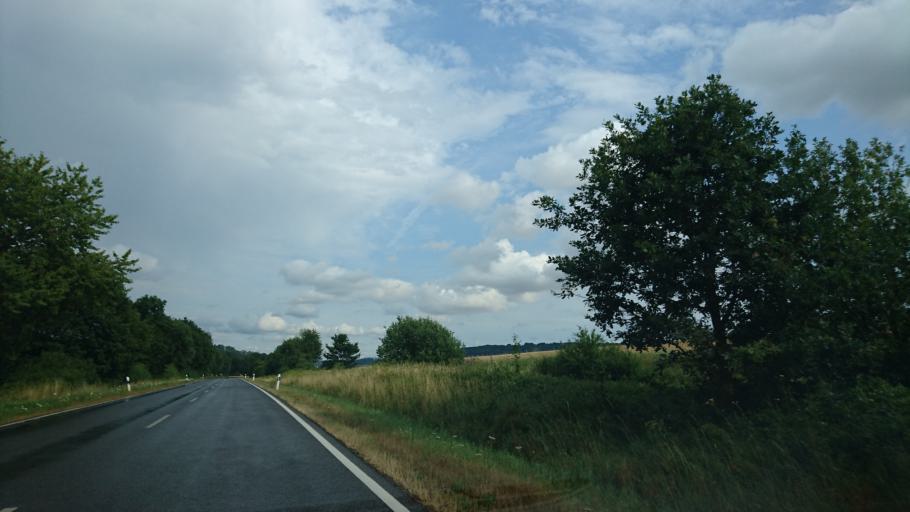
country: DE
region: Bavaria
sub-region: Regierungsbezirk Mittelfranken
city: Thalmassing
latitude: 49.1008
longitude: 11.2043
